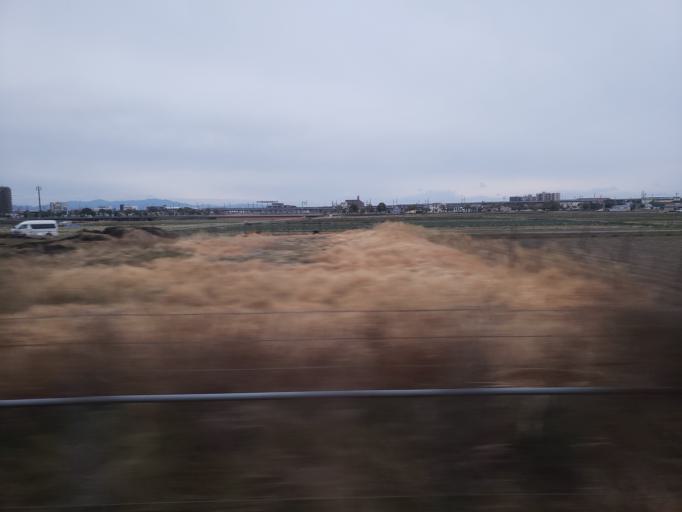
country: JP
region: Hyogo
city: Akashi
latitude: 34.6884
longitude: 134.9246
